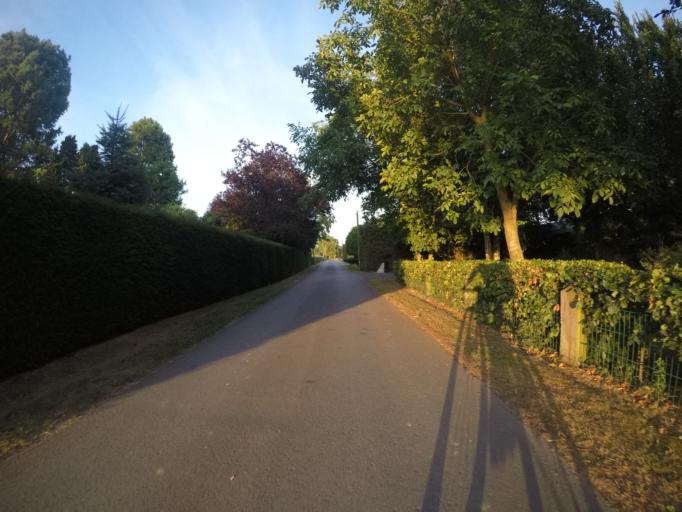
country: DE
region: North Rhine-Westphalia
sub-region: Regierungsbezirk Munster
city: Isselburg
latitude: 51.8548
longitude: 6.5167
